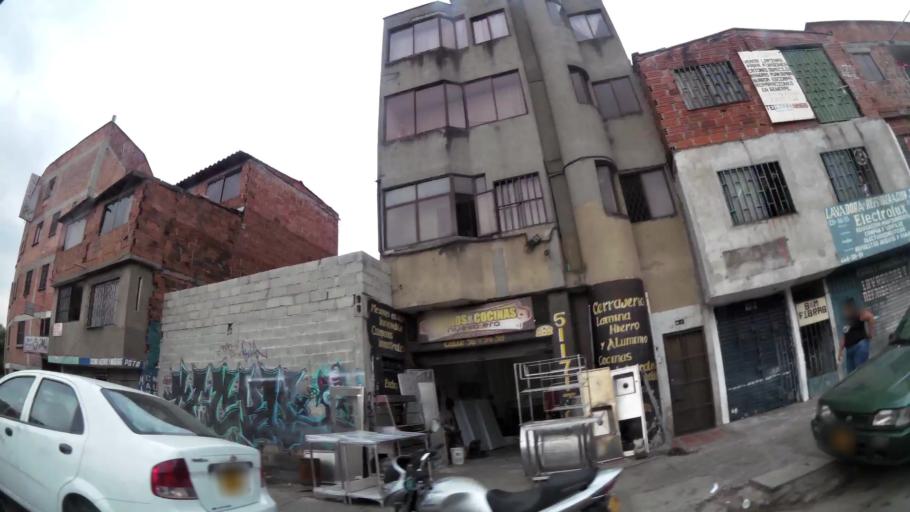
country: CO
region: Antioquia
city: Medellin
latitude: 6.2577
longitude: -75.5699
